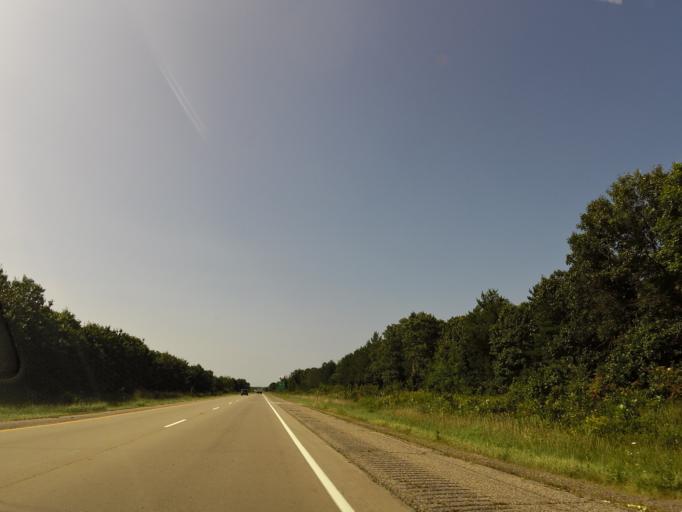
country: US
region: Wisconsin
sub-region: Columbia County
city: Wisconsin Dells
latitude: 43.7059
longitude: -89.8733
